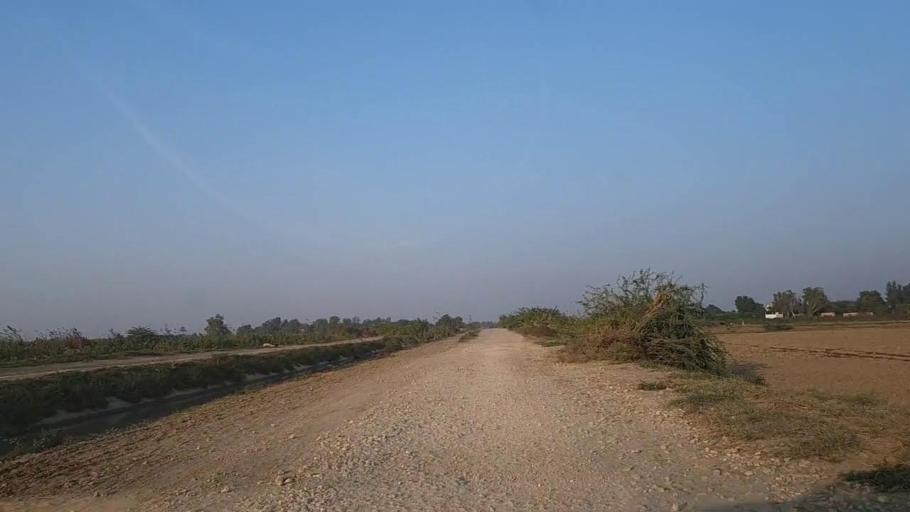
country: PK
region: Sindh
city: Mirpur Sakro
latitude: 24.2837
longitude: 67.6891
